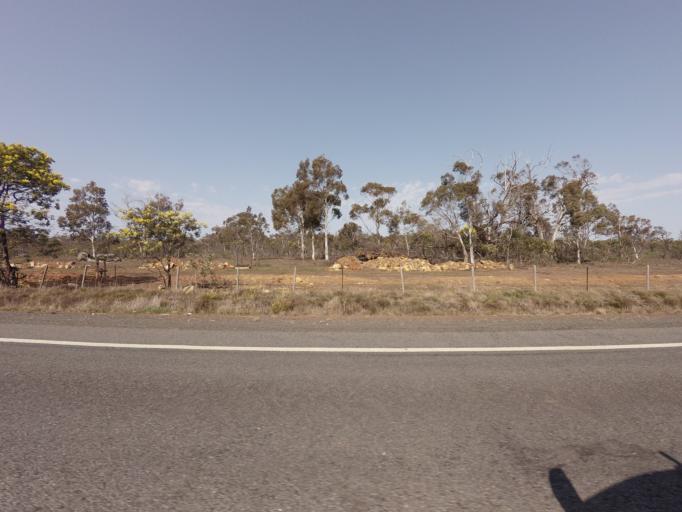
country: AU
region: Tasmania
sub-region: Northern Midlands
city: Evandale
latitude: -41.8306
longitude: 147.4881
